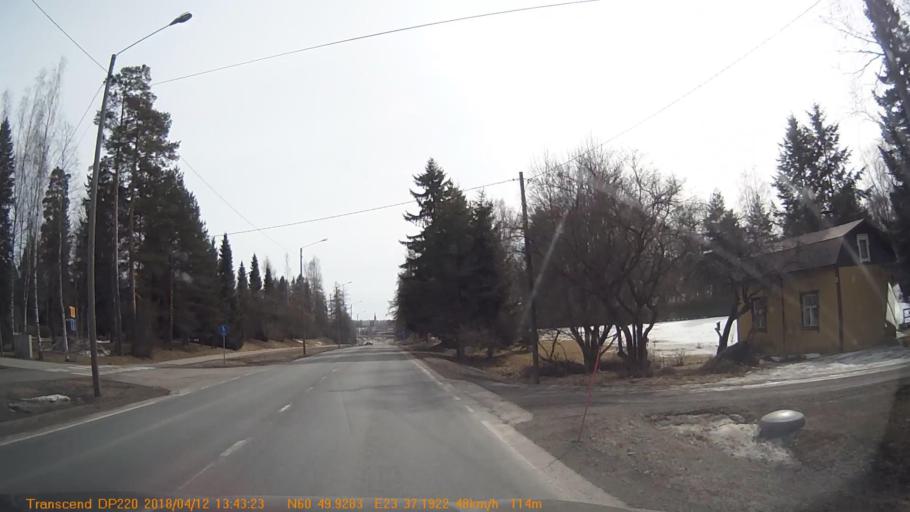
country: FI
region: Haeme
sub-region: Forssa
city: Forssa
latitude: 60.8318
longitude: 23.6201
